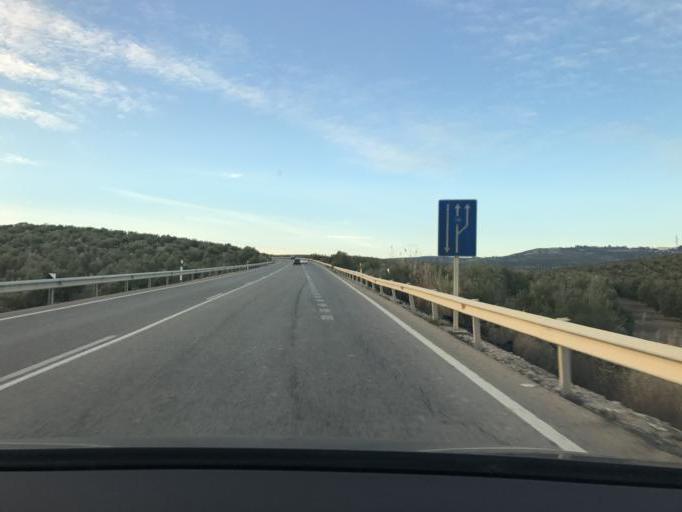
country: ES
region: Andalusia
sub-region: Provincia de Jaen
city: Ubeda
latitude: 37.9676
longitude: -3.3653
